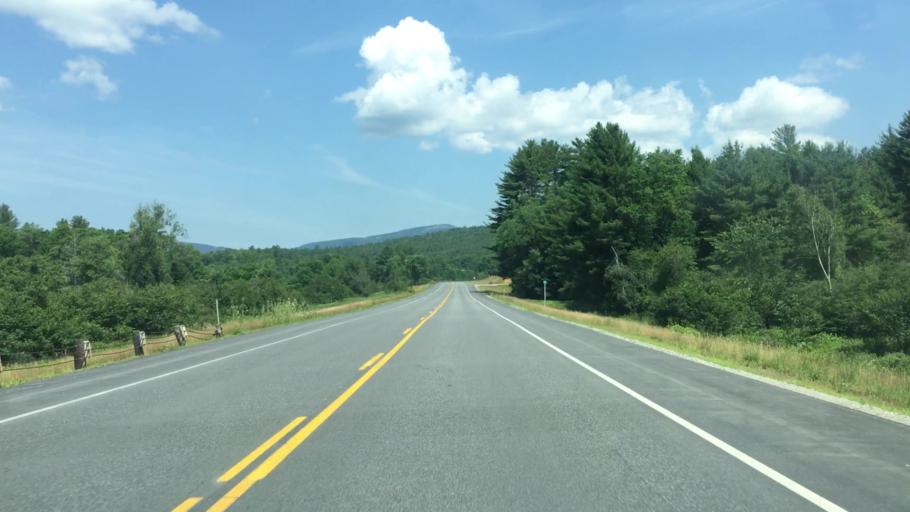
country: US
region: New Hampshire
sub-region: Sullivan County
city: Newport
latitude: 43.4075
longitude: -72.1861
